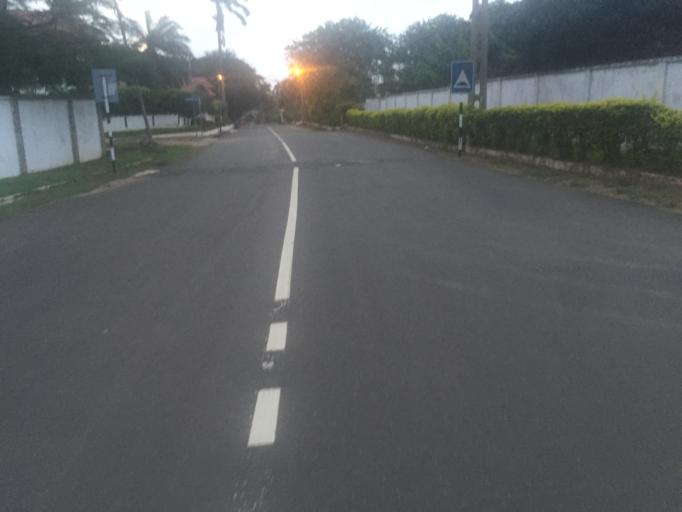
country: GH
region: Greater Accra
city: Dome
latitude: 5.6050
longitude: -0.2287
